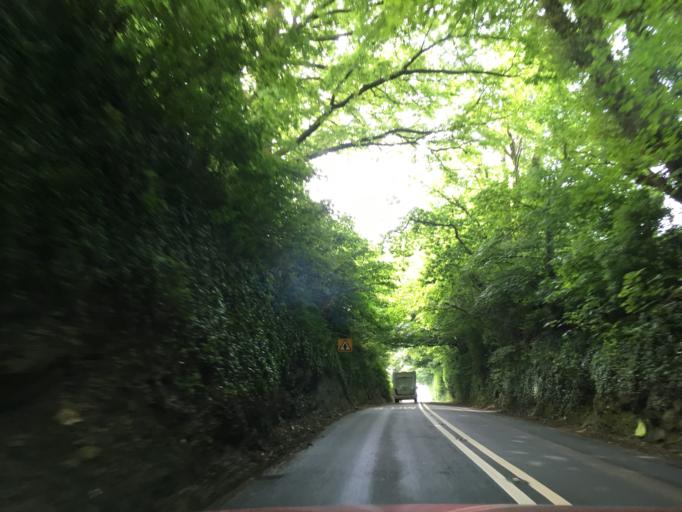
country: GB
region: England
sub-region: Devon
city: Totnes
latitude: 50.4233
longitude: -3.6963
